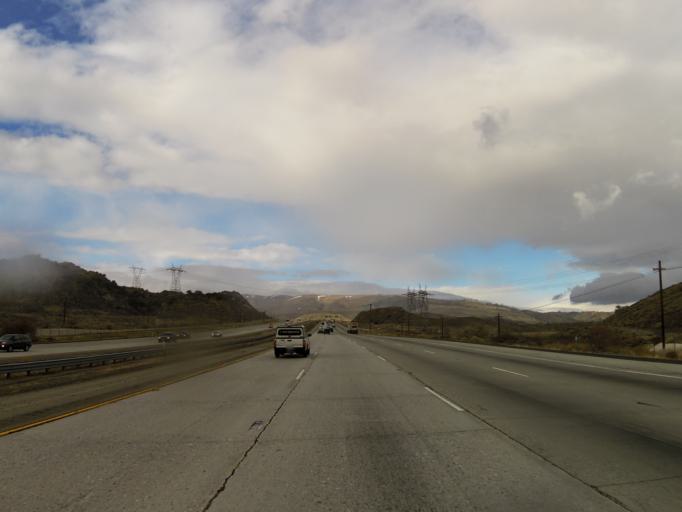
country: US
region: California
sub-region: Kern County
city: Lebec
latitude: 34.7489
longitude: -118.7955
